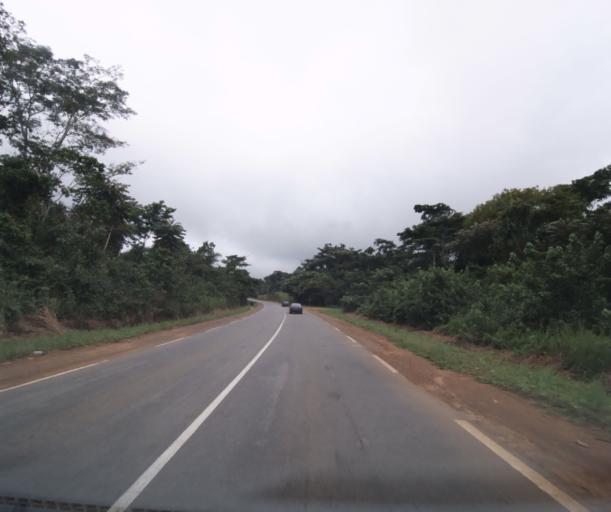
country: CM
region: Centre
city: Mbankomo
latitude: 3.7818
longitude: 11.2698
